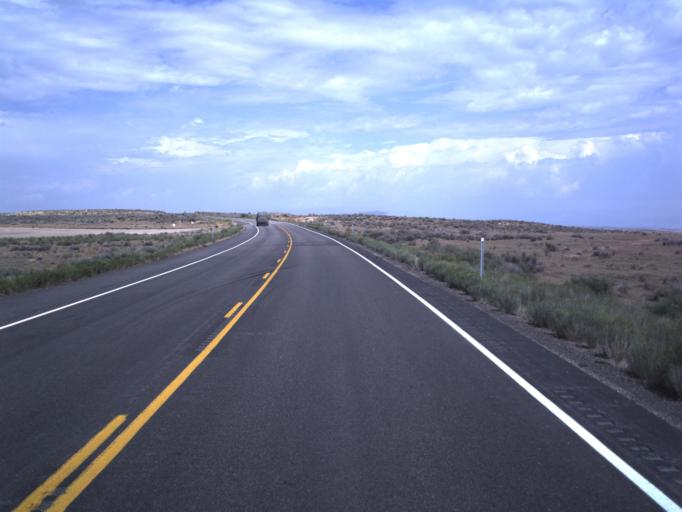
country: US
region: Utah
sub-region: Uintah County
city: Naples
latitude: 40.2478
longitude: -109.4221
